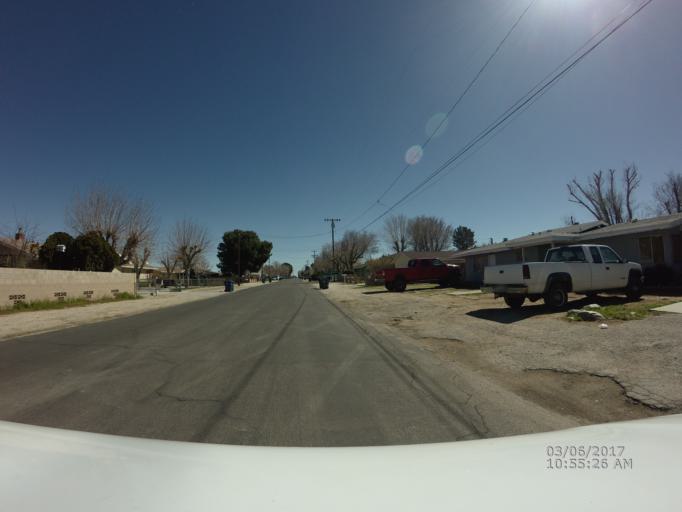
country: US
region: California
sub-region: Los Angeles County
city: Quartz Hill
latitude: 34.6566
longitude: -118.2273
